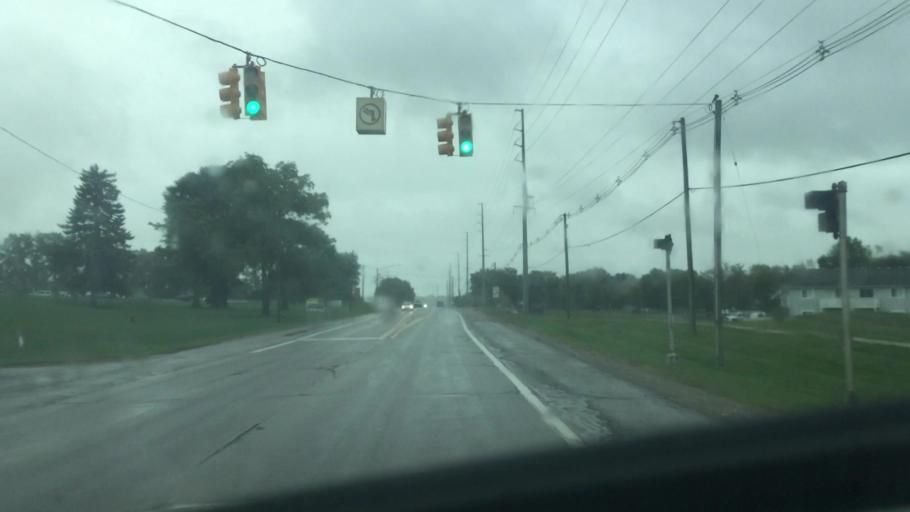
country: US
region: Michigan
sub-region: Livingston County
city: Brighton
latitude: 42.6325
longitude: -83.7662
